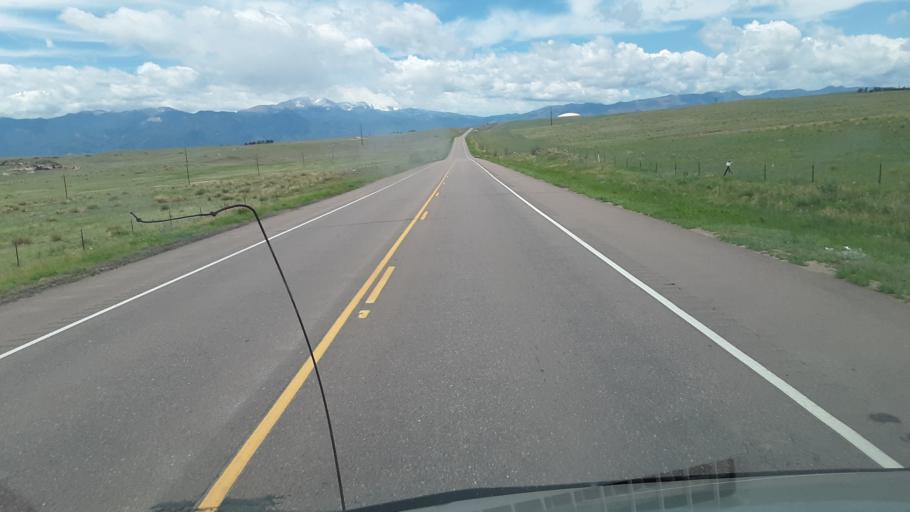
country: US
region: Colorado
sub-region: El Paso County
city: Cimarron Hills
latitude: 38.8358
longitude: -104.6500
